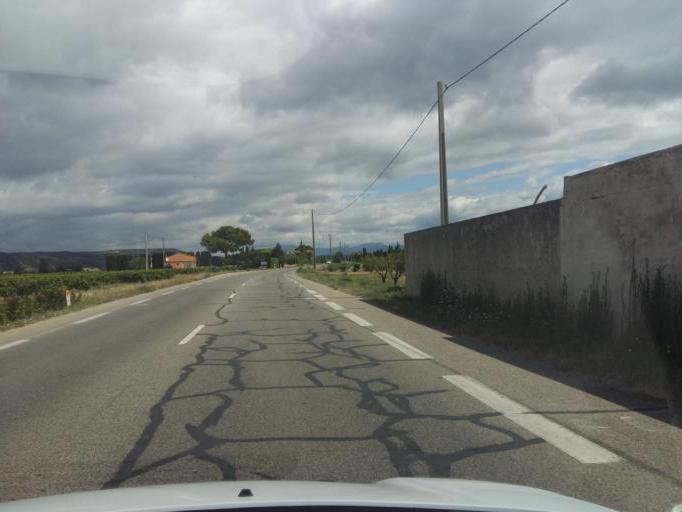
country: FR
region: Provence-Alpes-Cote d'Azur
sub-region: Departement du Vaucluse
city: Sablet
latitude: 44.2077
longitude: 5.0015
